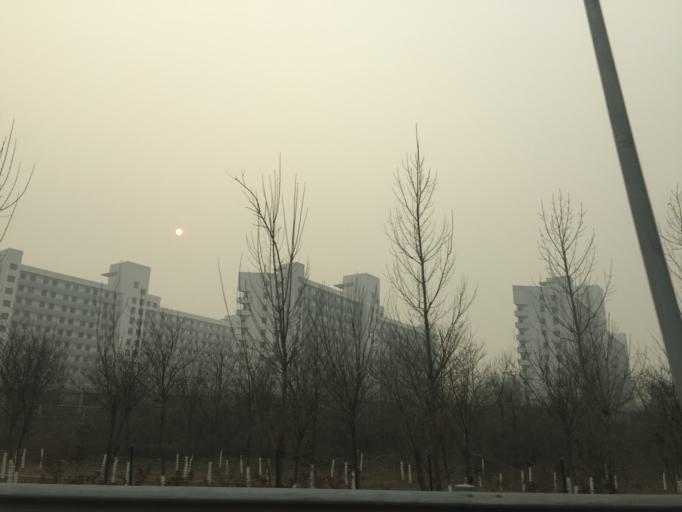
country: CN
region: Beijing
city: Qinghe
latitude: 40.0108
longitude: 116.3282
